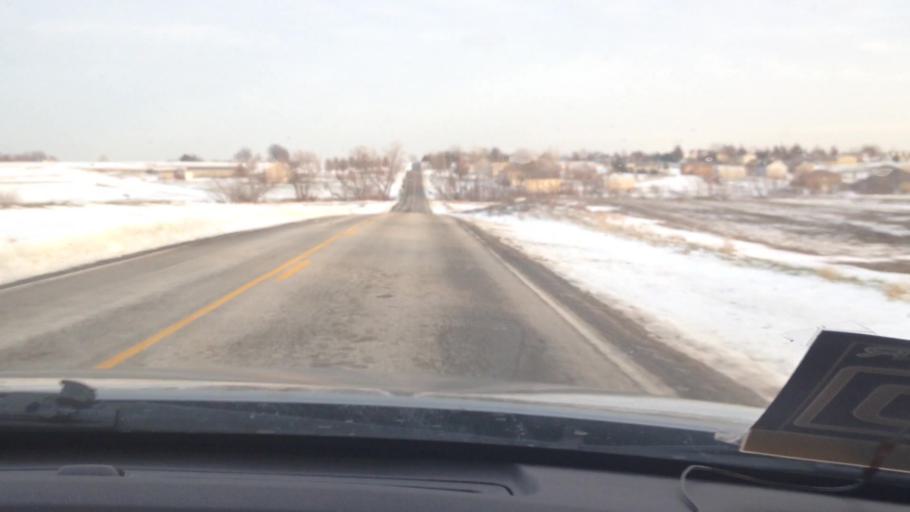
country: US
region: Kansas
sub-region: Leavenworth County
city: Lansing
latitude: 39.2304
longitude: -94.9690
